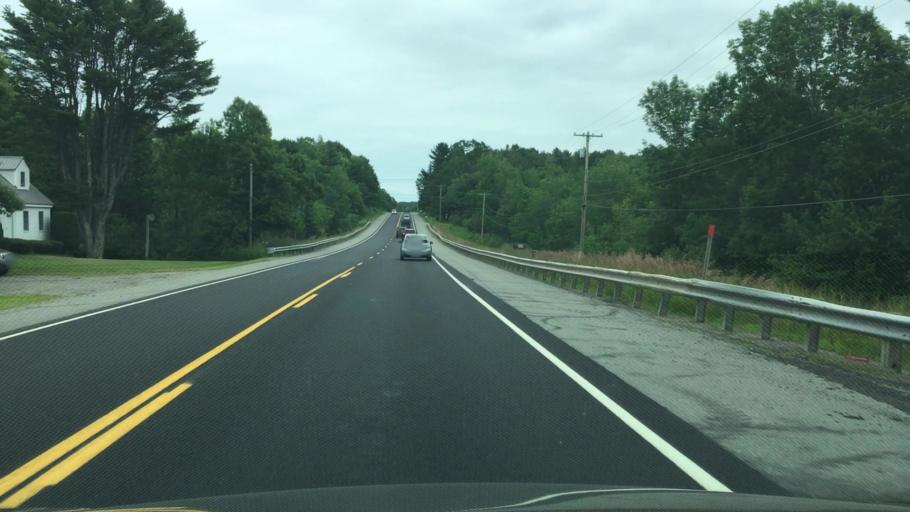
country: US
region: Maine
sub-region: Waldo County
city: Stockton Springs
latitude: 44.4986
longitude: -68.8315
